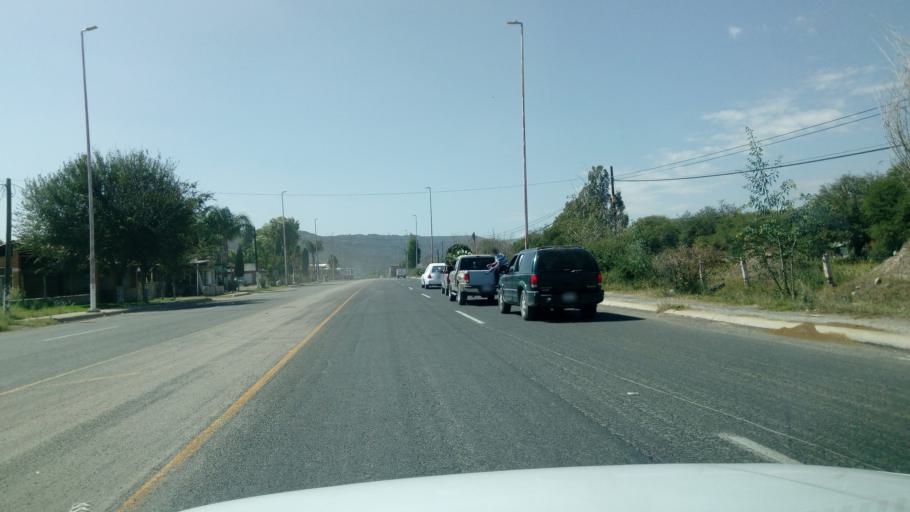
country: MX
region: Durango
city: Victoria de Durango
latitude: 23.9717
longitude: -104.7001
